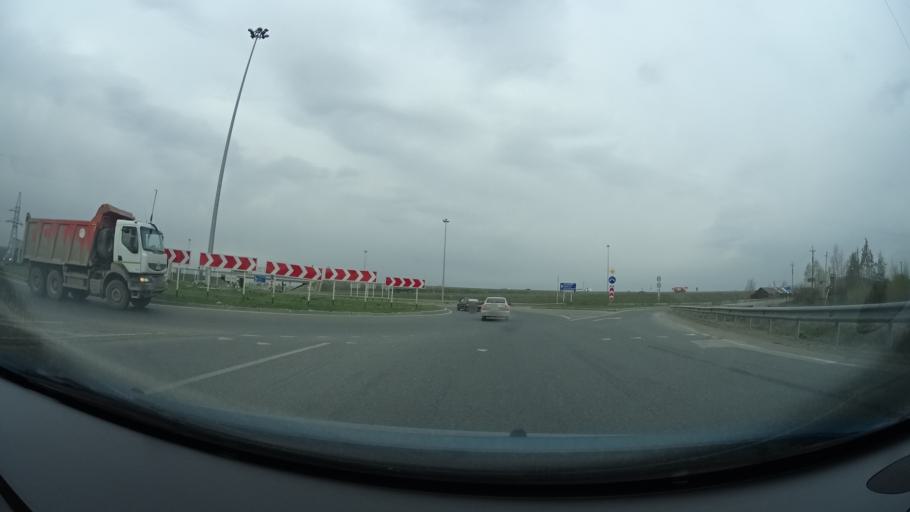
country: RU
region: Perm
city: Kondratovo
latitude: 58.0096
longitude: 56.0555
